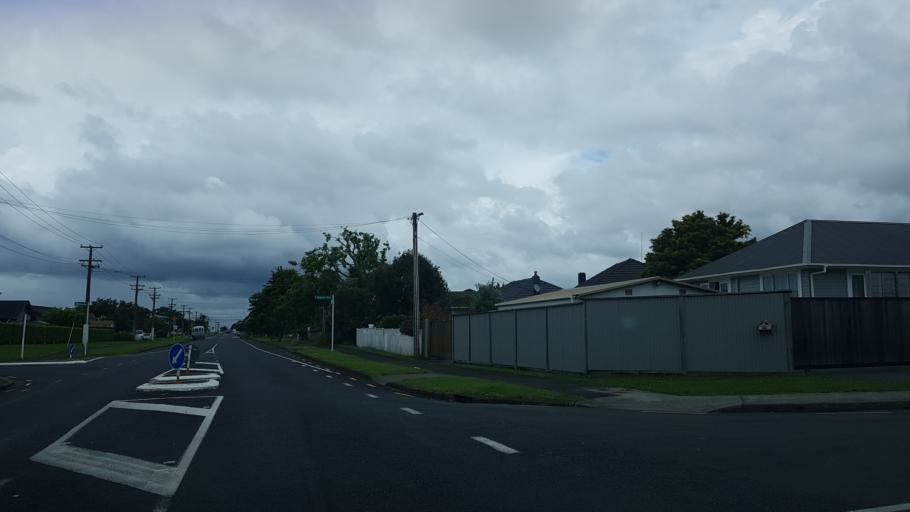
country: NZ
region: Auckland
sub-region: Auckland
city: Rosebank
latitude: -36.8336
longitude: 174.6564
